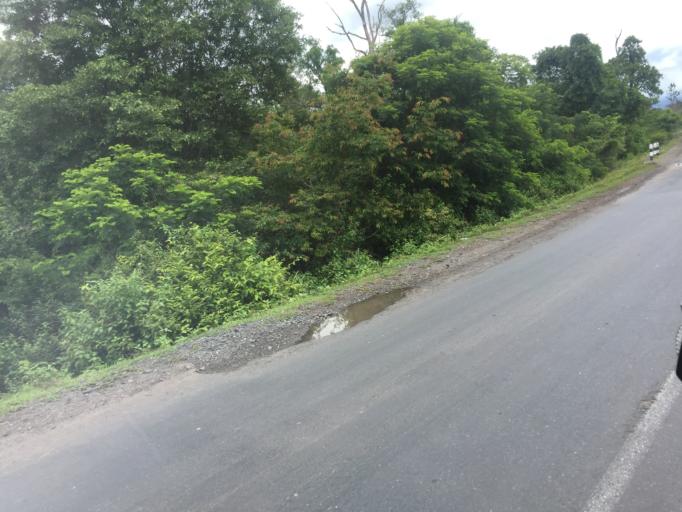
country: LA
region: Salavan
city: Salavan
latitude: 15.8372
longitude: 106.3882
